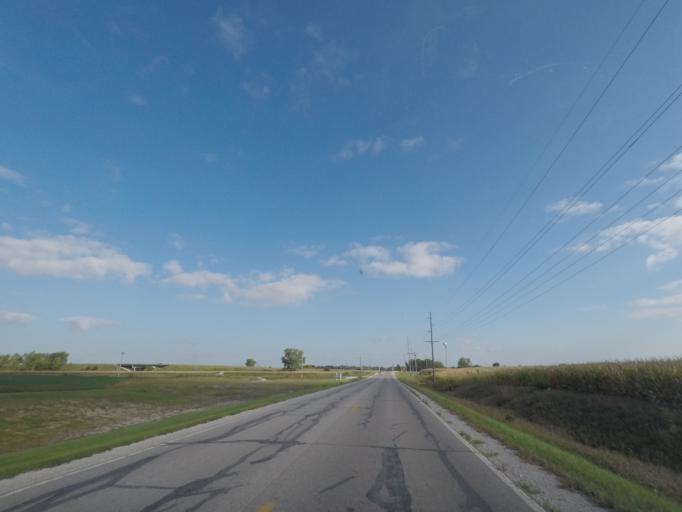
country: US
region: Iowa
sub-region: Story County
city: Nevada
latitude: 42.0034
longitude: -93.4628
